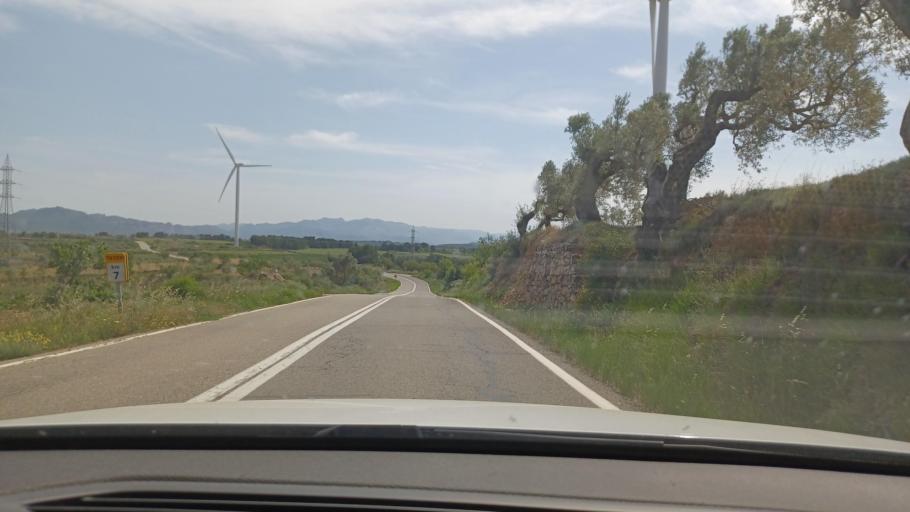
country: ES
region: Catalonia
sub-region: Provincia de Tarragona
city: Vilalba dels Arcs
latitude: 41.1028
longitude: 0.4174
